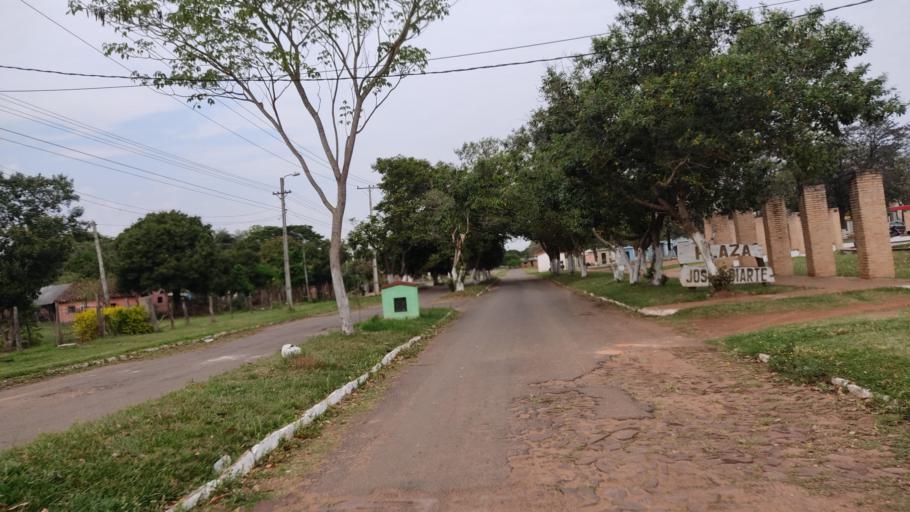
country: PY
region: Misiones
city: San Juan Bautista
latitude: -26.6693
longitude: -57.1526
